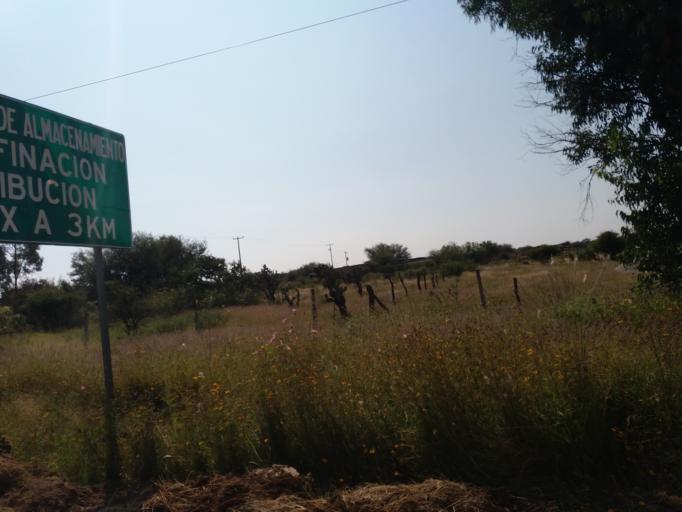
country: MX
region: Aguascalientes
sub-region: Aguascalientes
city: Penuelas (El Cienegal)
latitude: 21.7498
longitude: -102.2500
